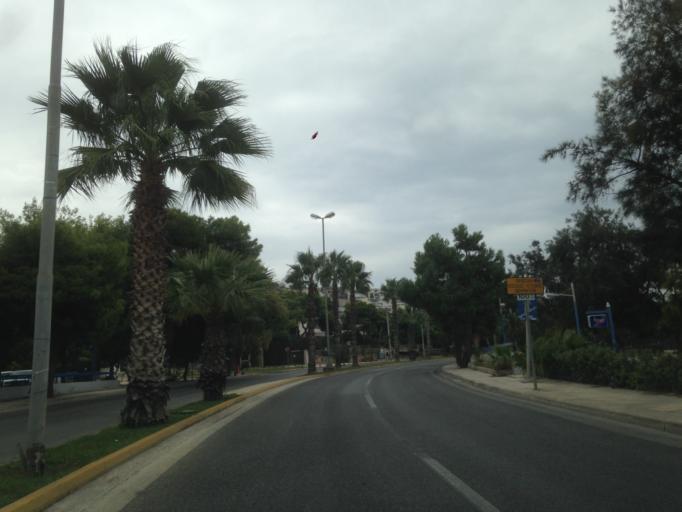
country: GR
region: Attica
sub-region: Nomarchia Anatolikis Attikis
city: Vouliagmeni
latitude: 37.8147
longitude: 23.7803
